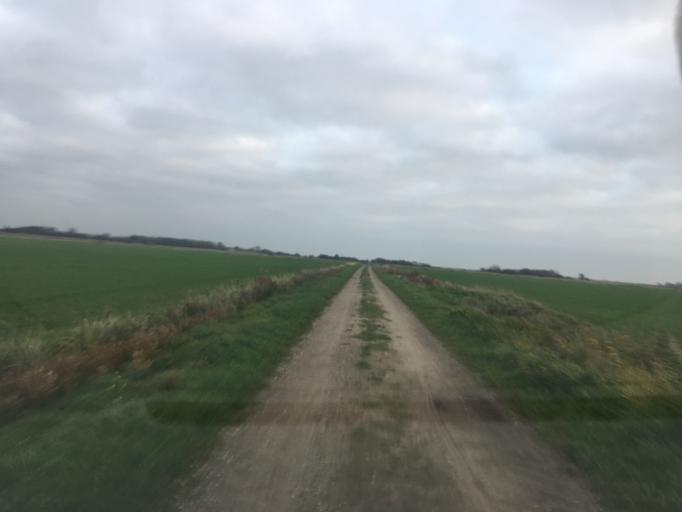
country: DE
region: Schleswig-Holstein
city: Rodenas
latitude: 54.9521
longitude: 8.7371
